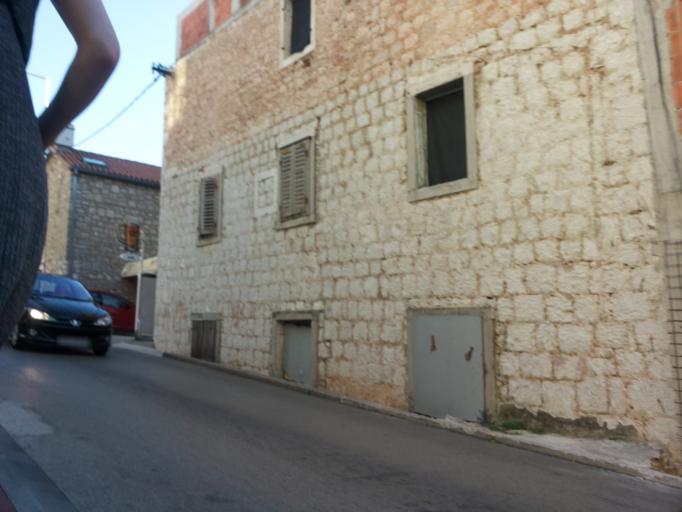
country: HR
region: Splitsko-Dalmatinska
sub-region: Grad Makarska
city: Makarska
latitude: 43.2953
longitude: 17.0205
